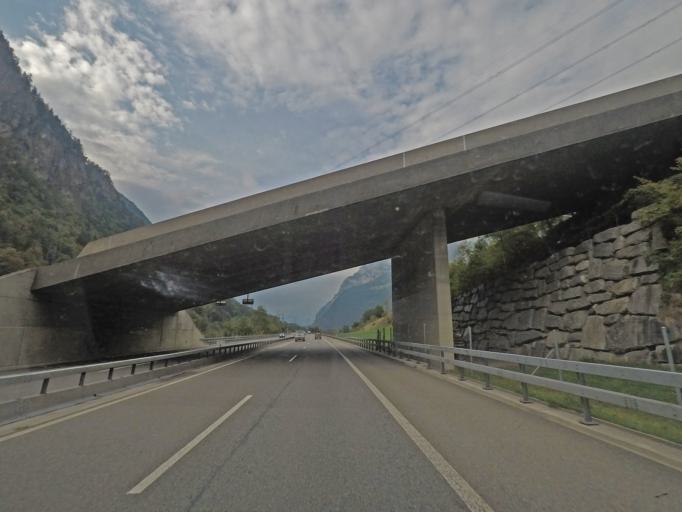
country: CH
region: Uri
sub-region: Uri
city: Silenen
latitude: 46.7838
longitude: 8.6688
